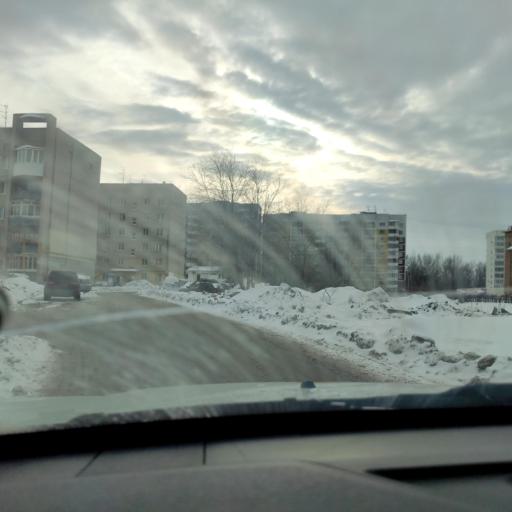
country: RU
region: Samara
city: Rozhdestveno
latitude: 53.1429
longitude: 50.0472
